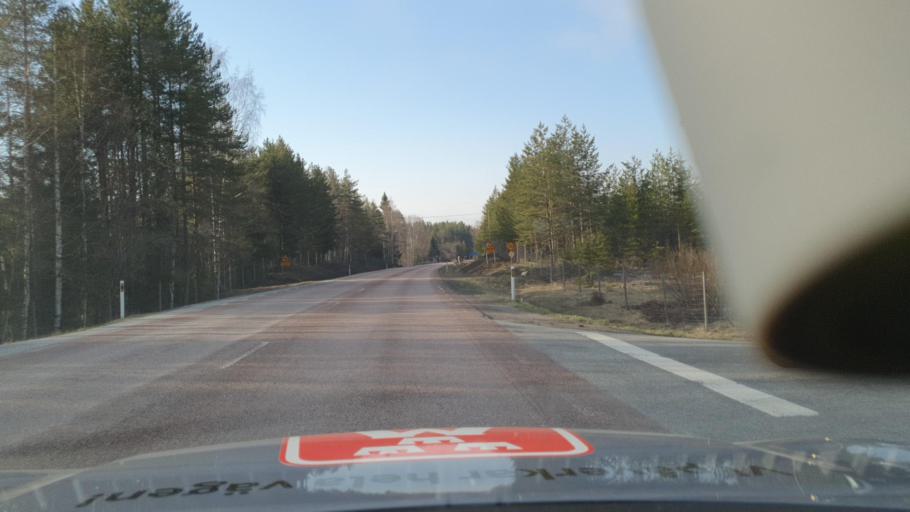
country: SE
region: Vaesterbotten
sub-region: Skelleftea Kommun
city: Burea
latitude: 64.6158
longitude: 21.1798
